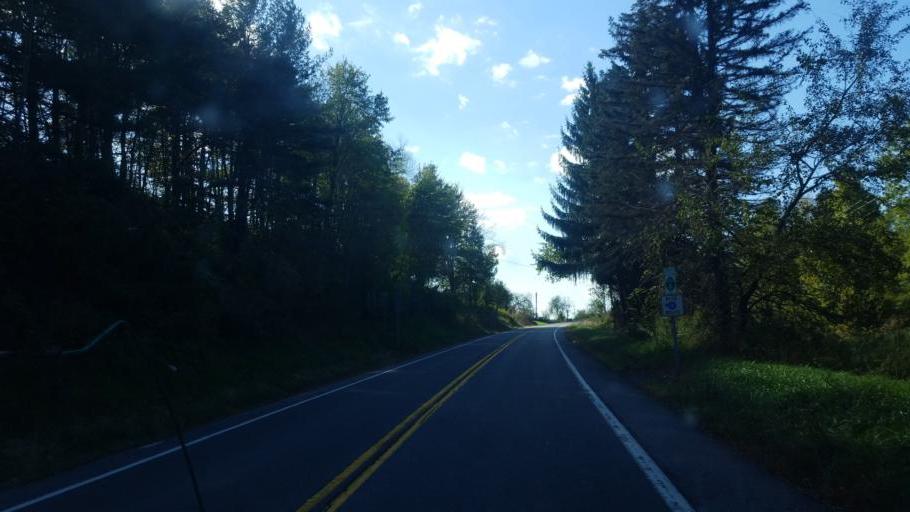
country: US
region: Pennsylvania
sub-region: Bedford County
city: Bedford
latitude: 40.1468
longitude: -78.5120
